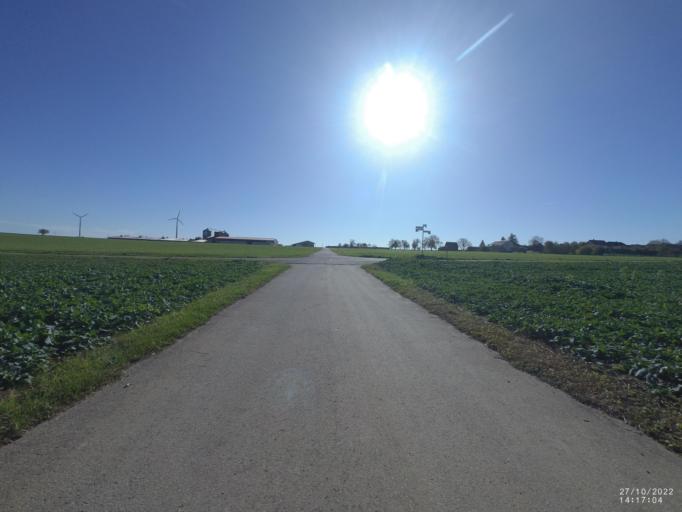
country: DE
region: Baden-Wuerttemberg
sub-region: Regierungsbezirk Stuttgart
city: Bohmenkirch
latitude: 48.6373
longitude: 9.9170
